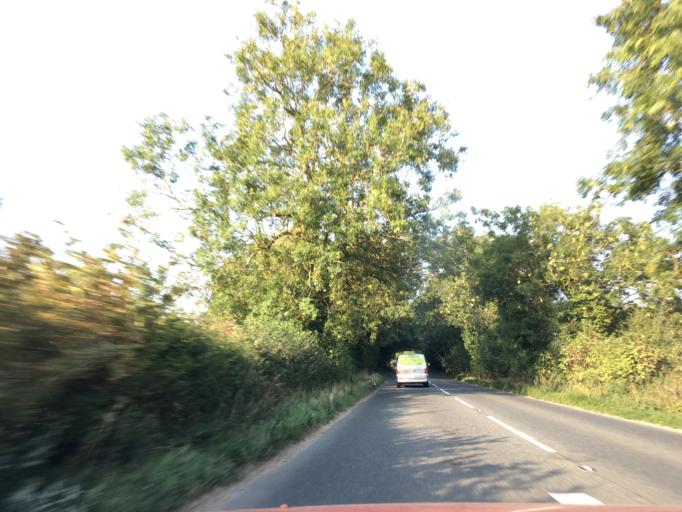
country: GB
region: England
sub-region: Gloucestershire
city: Stow on the Wold
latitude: 51.9029
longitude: -1.7454
